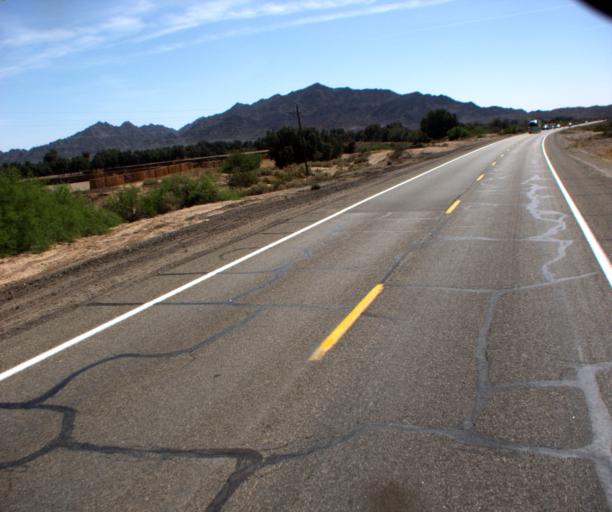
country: US
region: Arizona
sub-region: Yuma County
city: Fortuna Foothills
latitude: 32.7797
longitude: -114.3833
